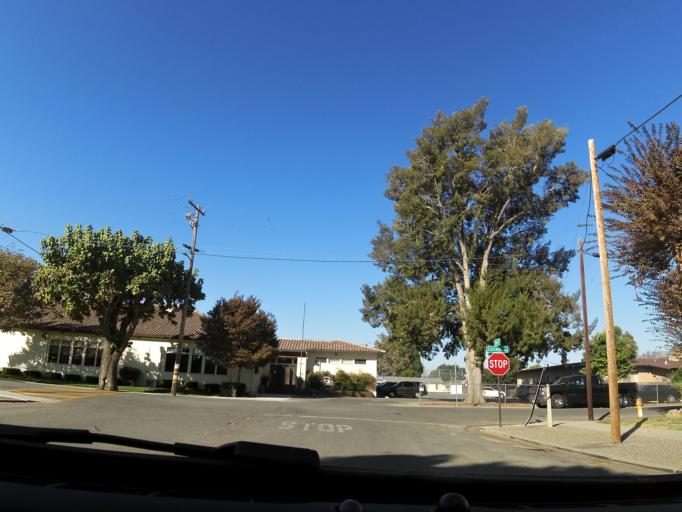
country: US
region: California
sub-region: San Benito County
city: Hollister
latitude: 36.8506
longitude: -121.4090
